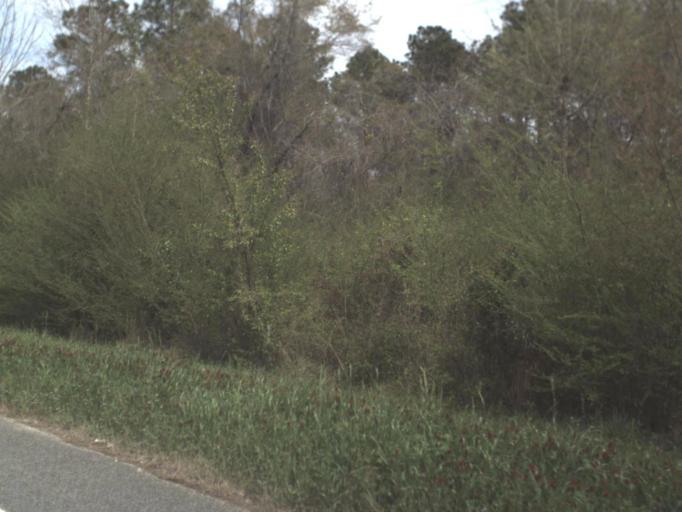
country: US
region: Florida
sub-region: Washington County
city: Chipley
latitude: 30.8629
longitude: -85.4936
